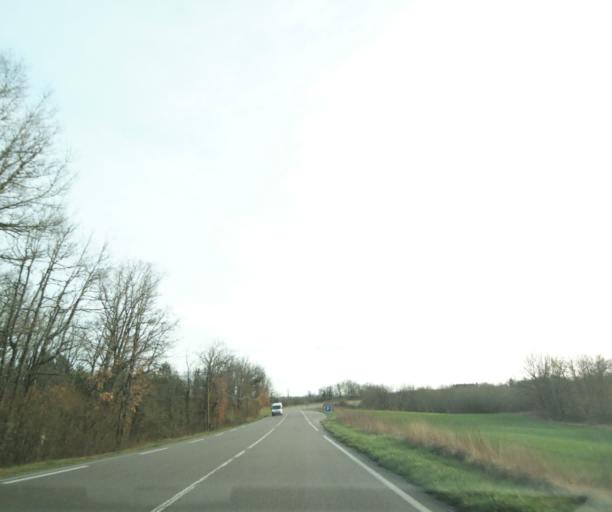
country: FR
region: Midi-Pyrenees
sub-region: Departement du Lot
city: Souillac
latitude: 44.9764
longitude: 1.5078
